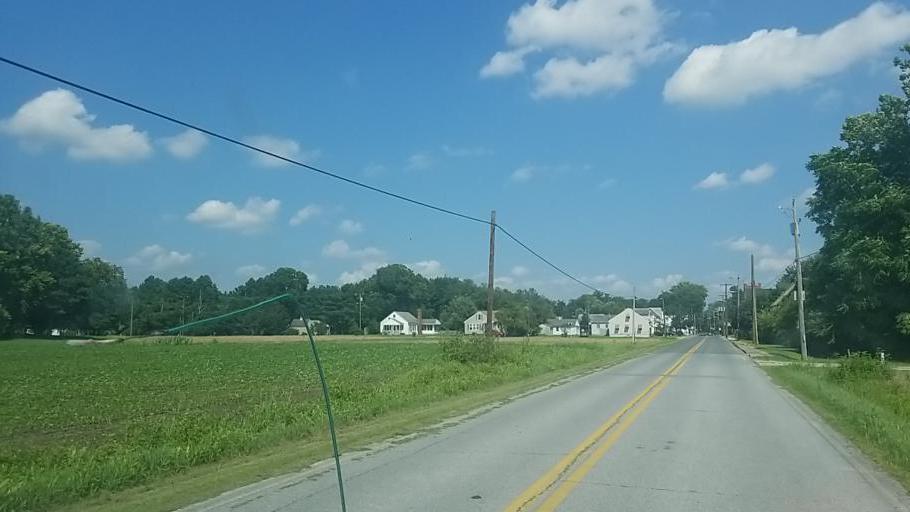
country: US
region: Maryland
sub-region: Wicomico County
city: Hebron
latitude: 38.4597
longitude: -75.7626
